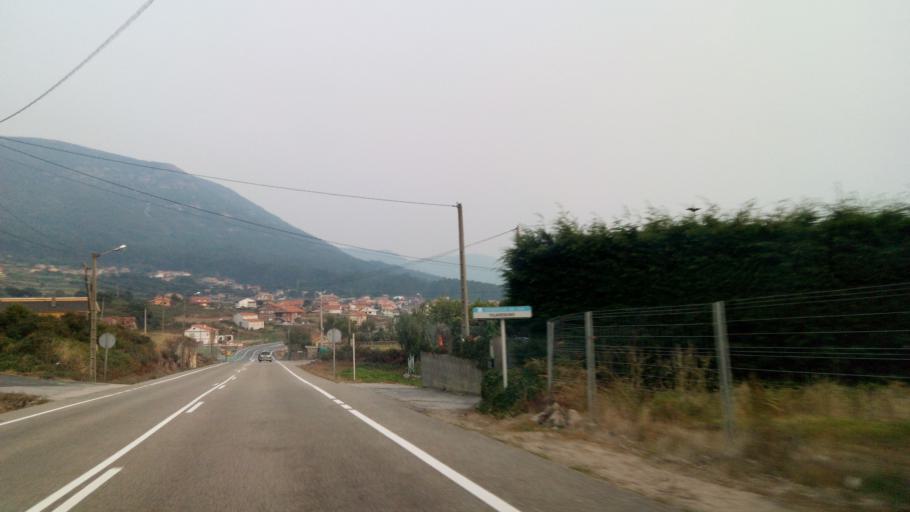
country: ES
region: Galicia
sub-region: Provincia de Pontevedra
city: Oia
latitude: 42.0435
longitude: -8.8828
